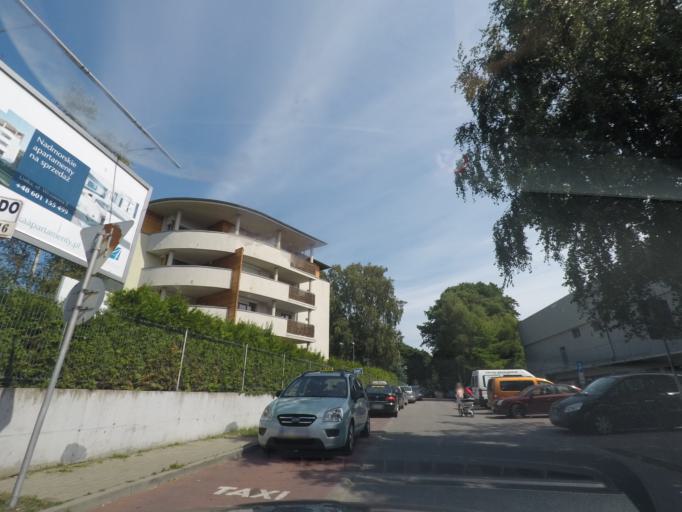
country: PL
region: Pomeranian Voivodeship
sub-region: Powiat slupski
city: Ustka
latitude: 54.5829
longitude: 16.8674
